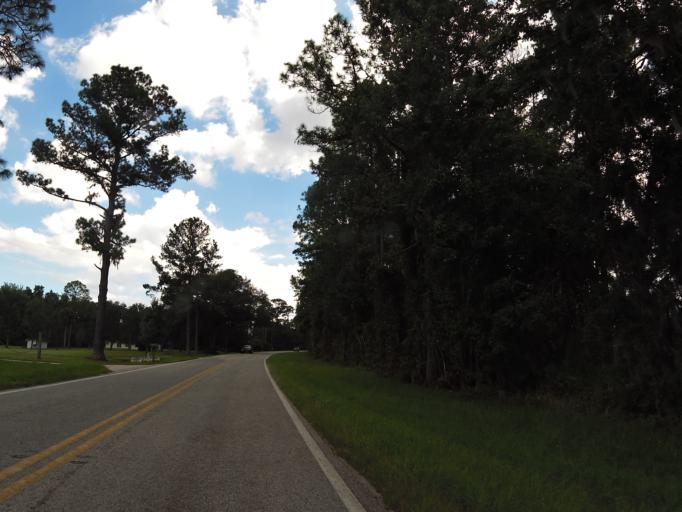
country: US
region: Florida
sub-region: Putnam County
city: East Palatka
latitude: 29.7676
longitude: -81.4766
